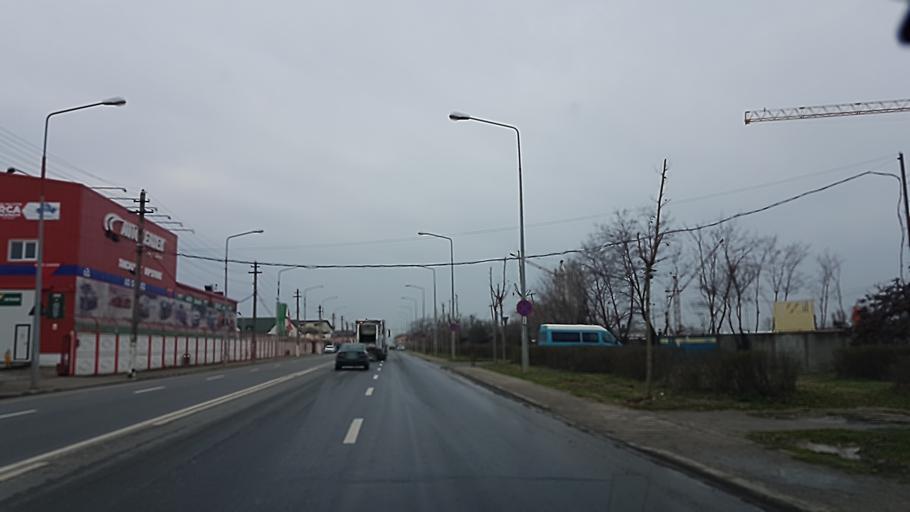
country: RO
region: Ilfov
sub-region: Comuna Glina
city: Catelu
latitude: 44.4265
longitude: 26.2207
